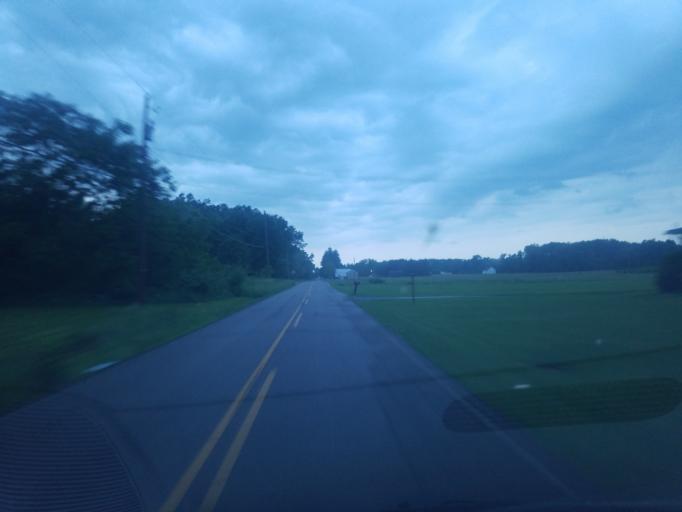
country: US
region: Ohio
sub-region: Mahoning County
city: Canfield
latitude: 40.9727
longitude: -80.7755
